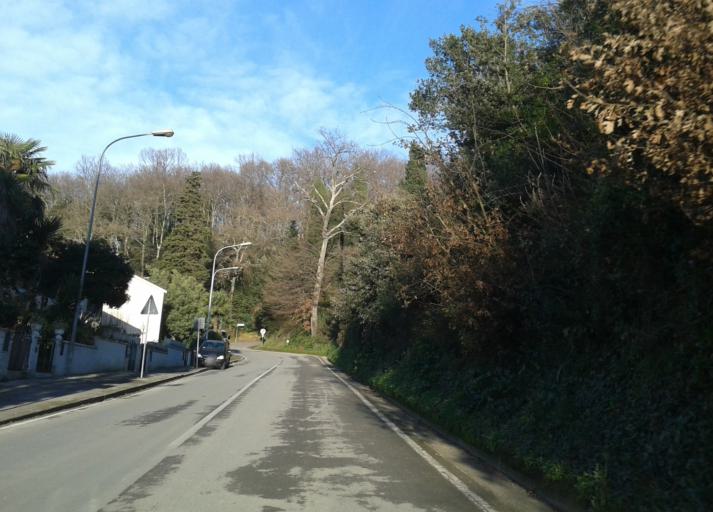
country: IT
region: Tuscany
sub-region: Provincia di Livorno
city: Collesalvetti
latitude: 43.5785
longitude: 10.4442
